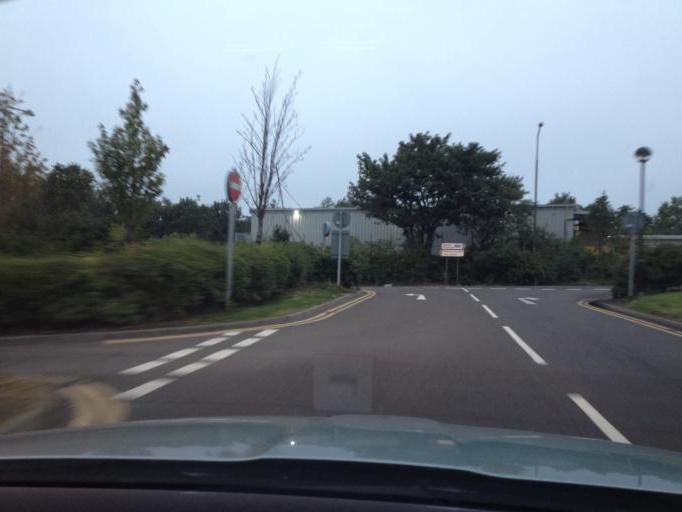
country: GB
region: Scotland
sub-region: West Lothian
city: Livingston
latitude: 55.8931
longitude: -3.5240
